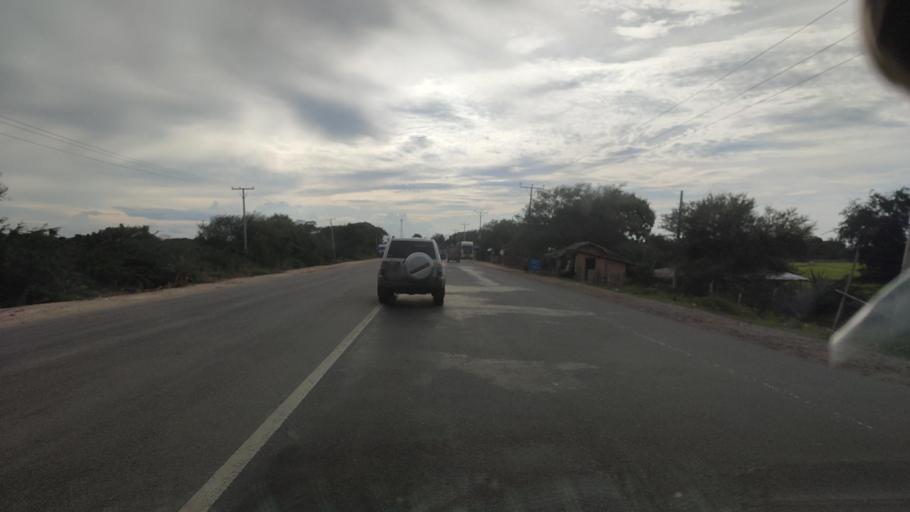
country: MM
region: Mandalay
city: Kyaukse
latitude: 21.3511
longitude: 96.1313
